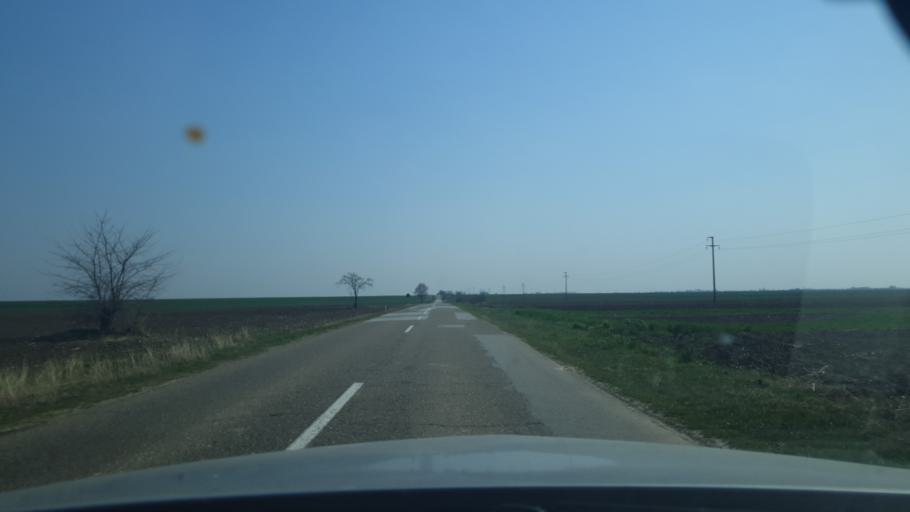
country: RS
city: Sasinci
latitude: 45.0414
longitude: 19.7311
